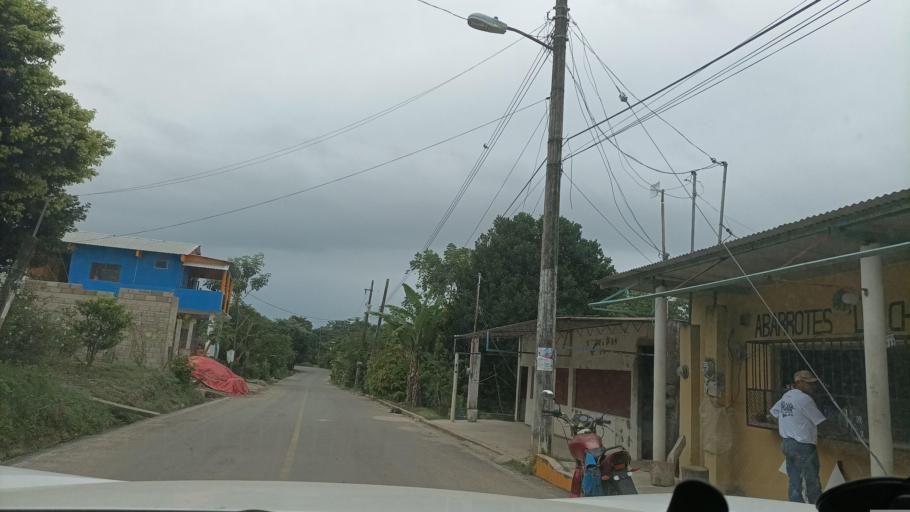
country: MX
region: Veracruz
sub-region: Jaltipan
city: Las Lomas de Tacamichapan
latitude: 17.8660
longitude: -94.7098
